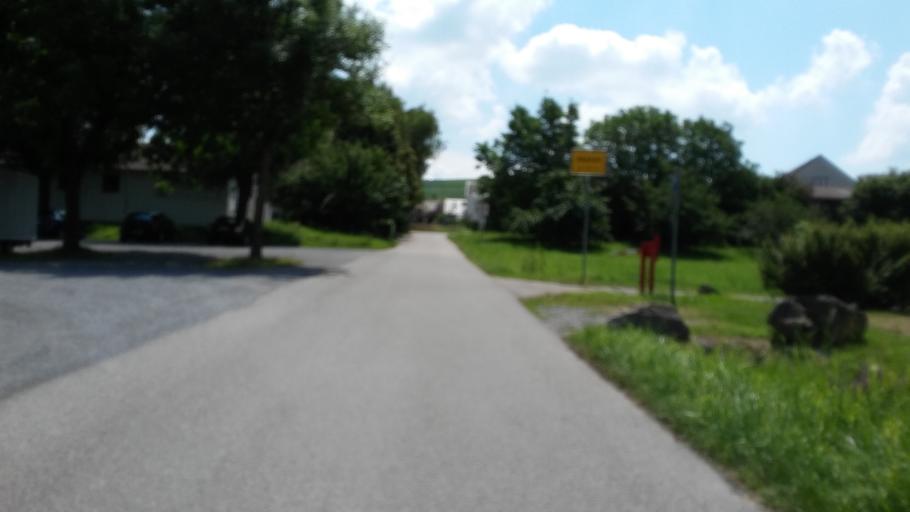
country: DE
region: Baden-Wuerttemberg
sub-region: Regierungsbezirk Stuttgart
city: Abstatt
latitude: 49.0701
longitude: 9.2991
